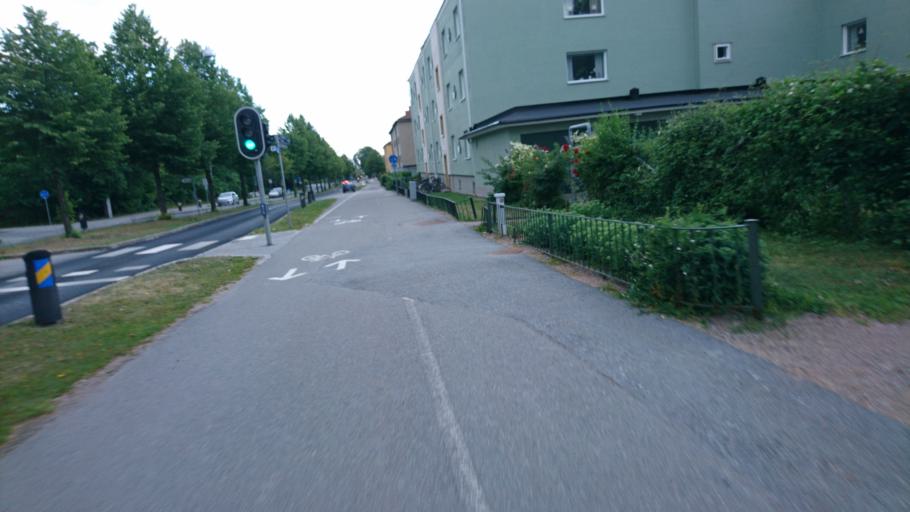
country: SE
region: Uppsala
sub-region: Uppsala Kommun
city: Gamla Uppsala
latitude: 59.8770
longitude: 17.6234
